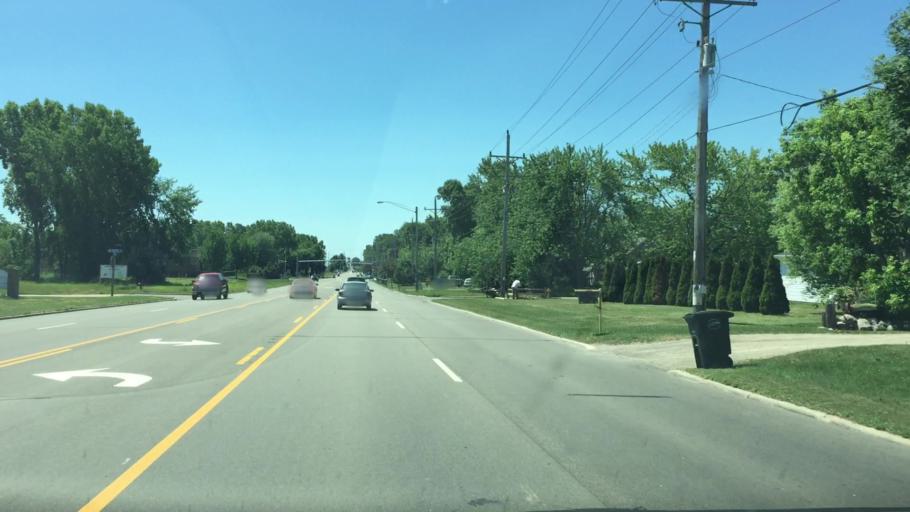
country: US
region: Wisconsin
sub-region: Outagamie County
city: Appleton
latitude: 44.2215
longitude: -88.4042
